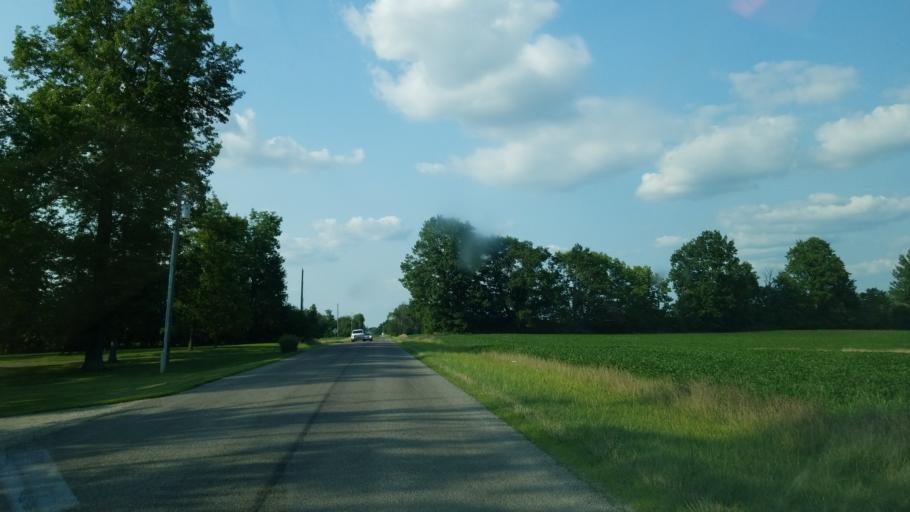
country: US
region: Ohio
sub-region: Union County
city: Marysville
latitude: 40.3006
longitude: -83.2966
